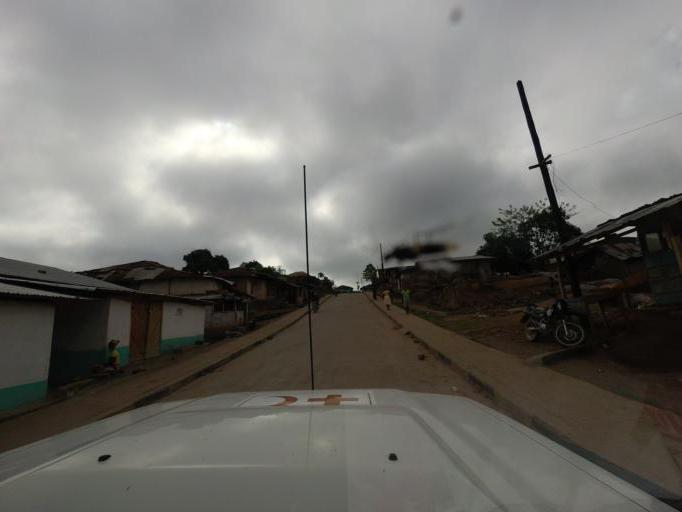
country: LR
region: Lofa
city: Voinjama
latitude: 8.4234
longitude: -9.7530
